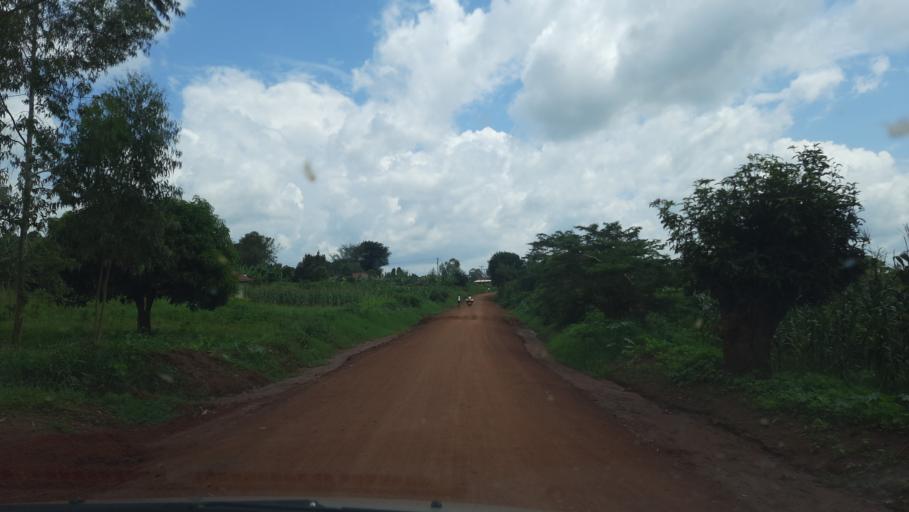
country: UG
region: Western Region
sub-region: Kiryandongo District
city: Kiryandongo
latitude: 1.8143
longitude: 31.9954
